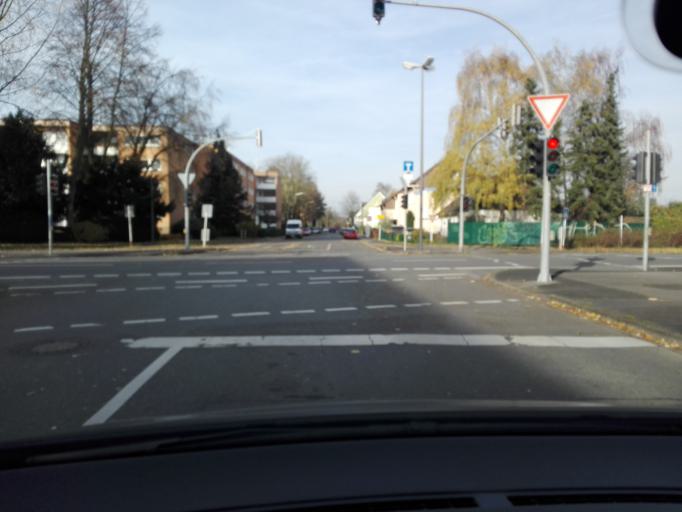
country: DE
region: North Rhine-Westphalia
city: Lanstrop
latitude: 51.5315
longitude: 7.5378
